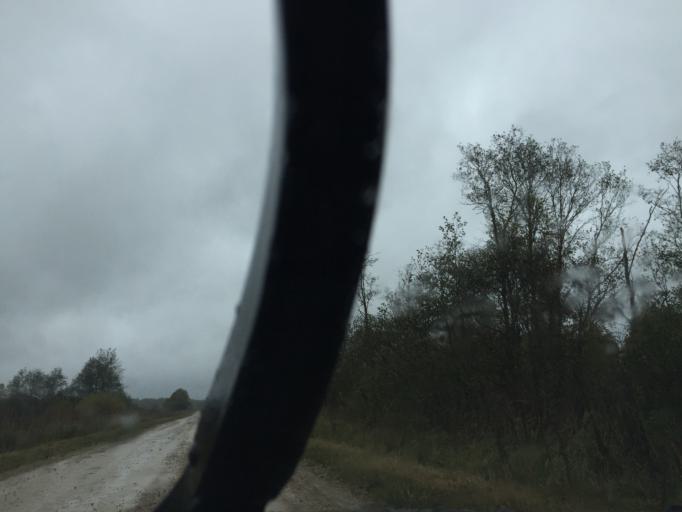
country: LV
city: Tireli
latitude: 56.7672
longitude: 23.5419
